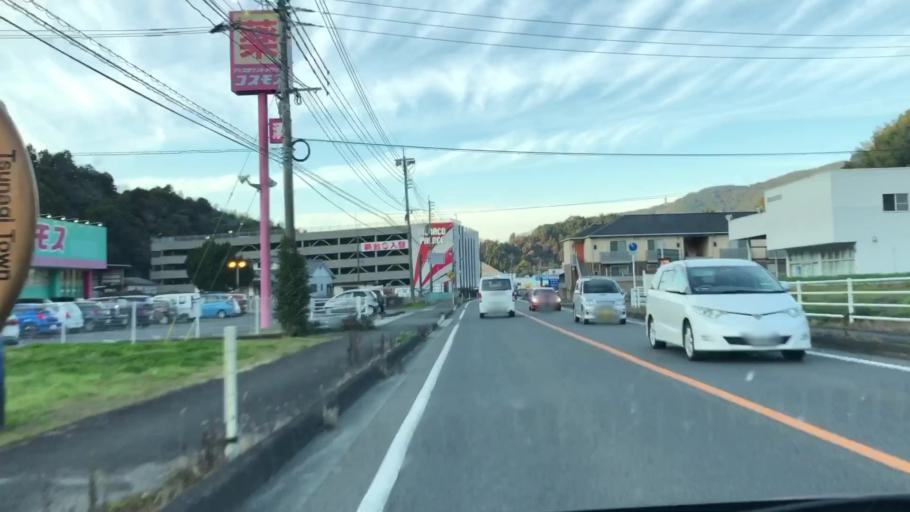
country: JP
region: Kumamoto
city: Minamata
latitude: 32.2214
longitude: 130.4380
